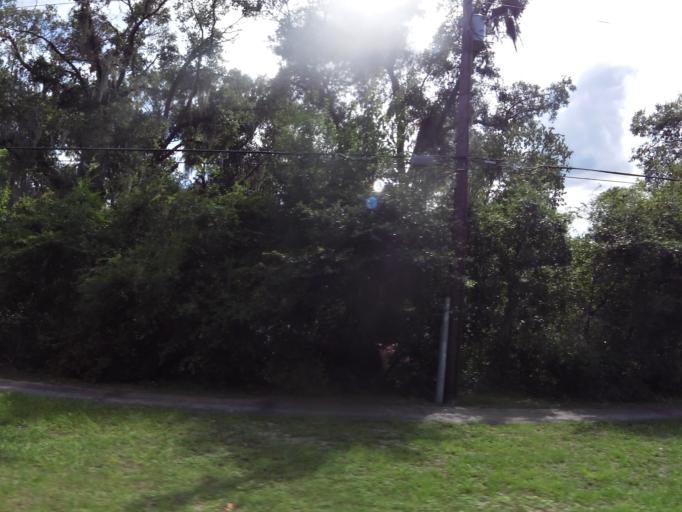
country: US
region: Florida
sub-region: Clay County
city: Lakeside
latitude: 30.1256
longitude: -81.7676
